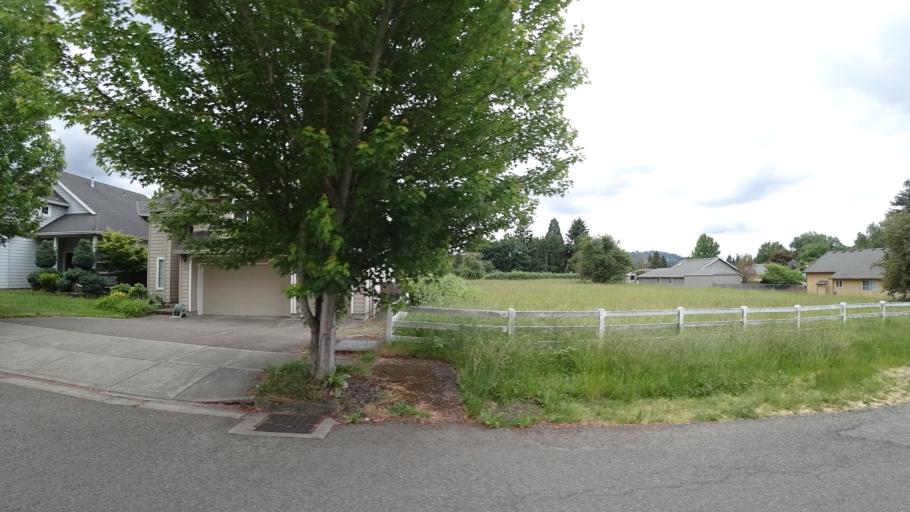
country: US
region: Oregon
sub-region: Clackamas County
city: Happy Valley
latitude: 45.4863
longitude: -122.5205
